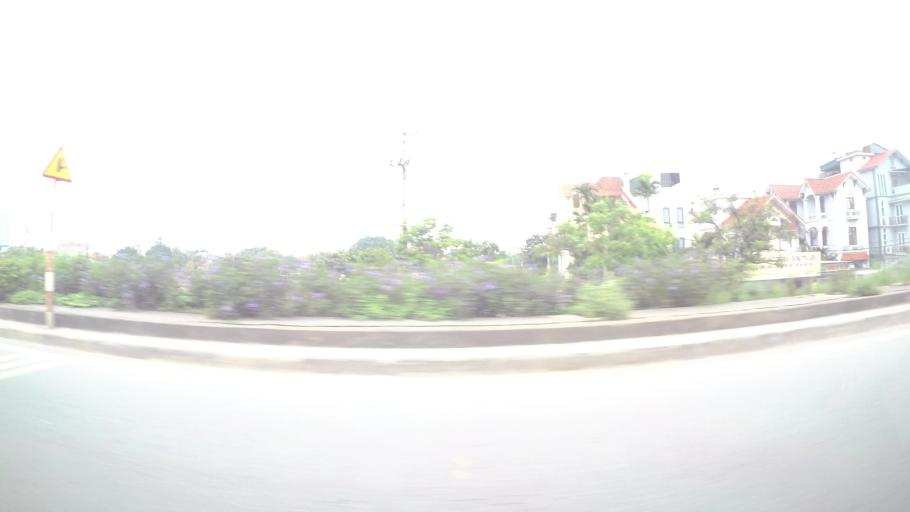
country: VN
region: Ha Noi
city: Hoan Kiem
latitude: 21.0572
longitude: 105.8655
